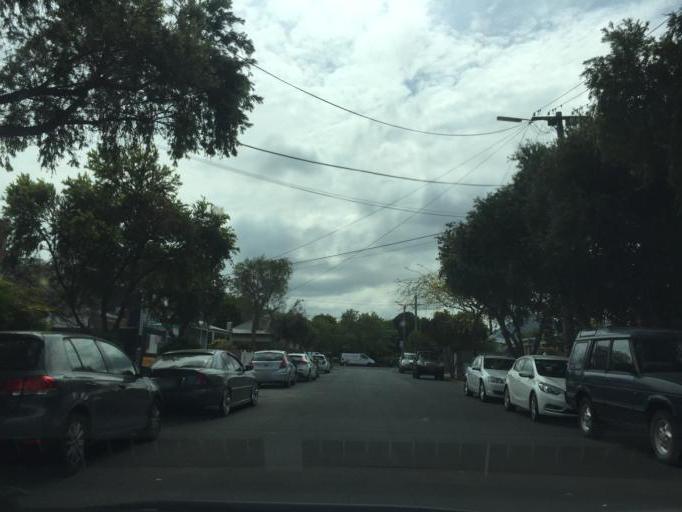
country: AU
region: Victoria
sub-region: Maribyrnong
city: Seddon
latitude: -37.8056
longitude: 144.8891
